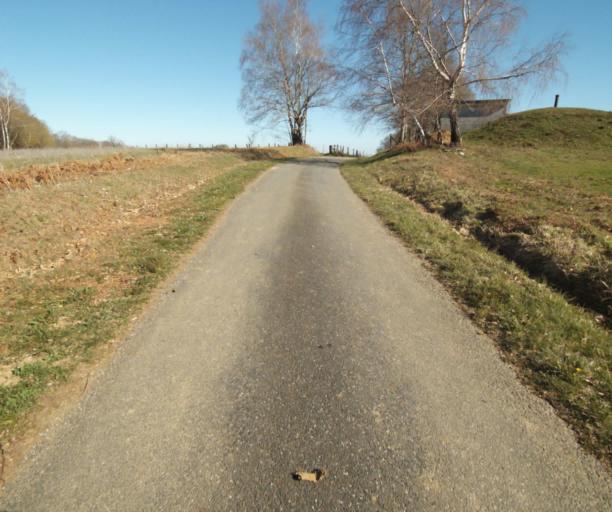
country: FR
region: Limousin
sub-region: Departement de la Correze
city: Seilhac
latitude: 45.3924
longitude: 1.6976
